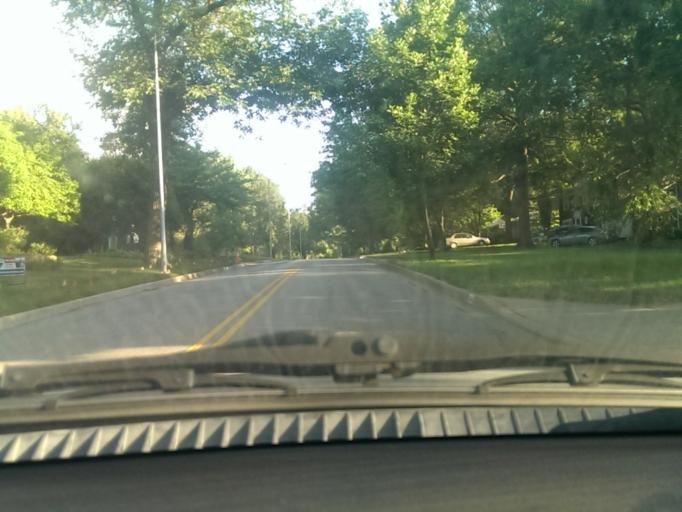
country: US
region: Kansas
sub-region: Johnson County
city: Mission Hills
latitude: 39.0105
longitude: -94.6078
